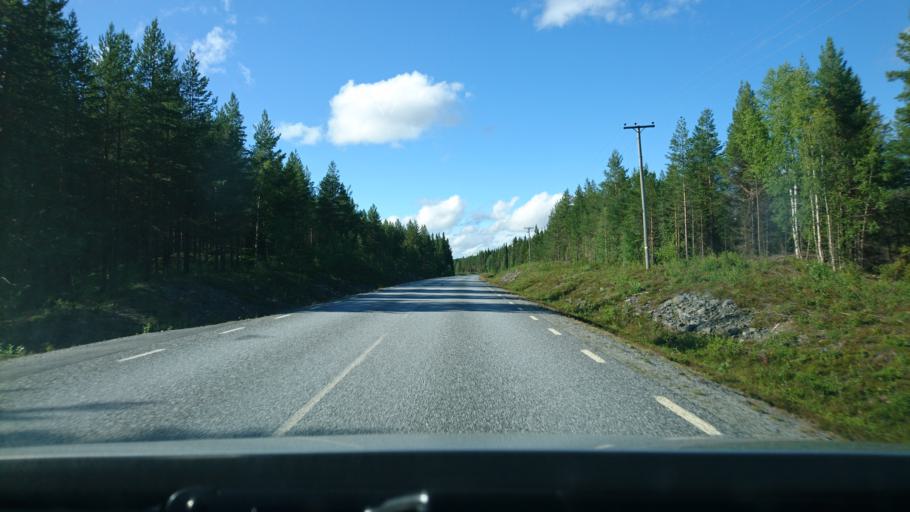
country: SE
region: Vaesterbotten
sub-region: Vilhelmina Kommun
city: Vilhelmina
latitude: 64.3759
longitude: 16.9045
